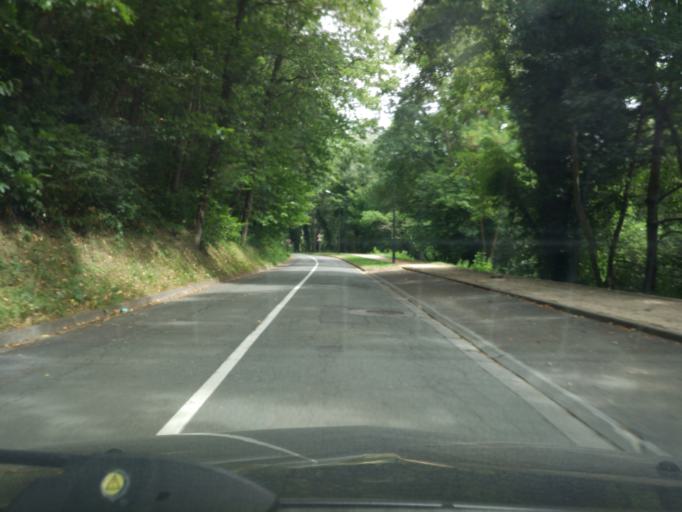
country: FR
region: Ile-de-France
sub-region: Departement de l'Essonne
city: Villiers-le-Bacle
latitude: 48.7196
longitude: 2.1216
